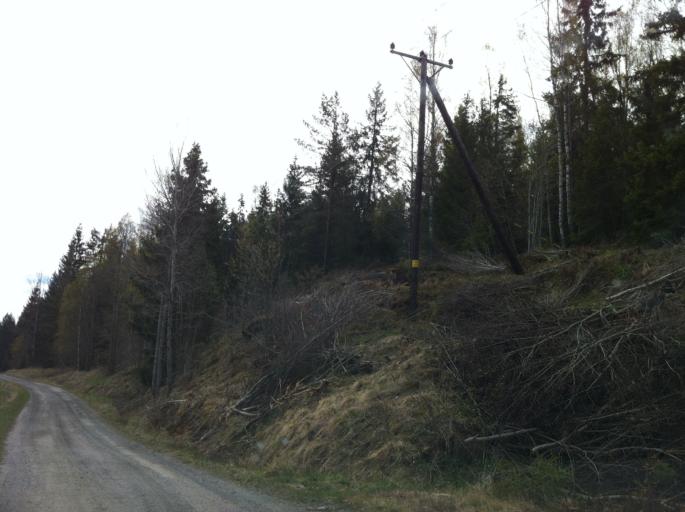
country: SE
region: OEstergoetland
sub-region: Valdemarsviks Kommun
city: Valdemarsvik
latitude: 58.1970
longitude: 16.6216
